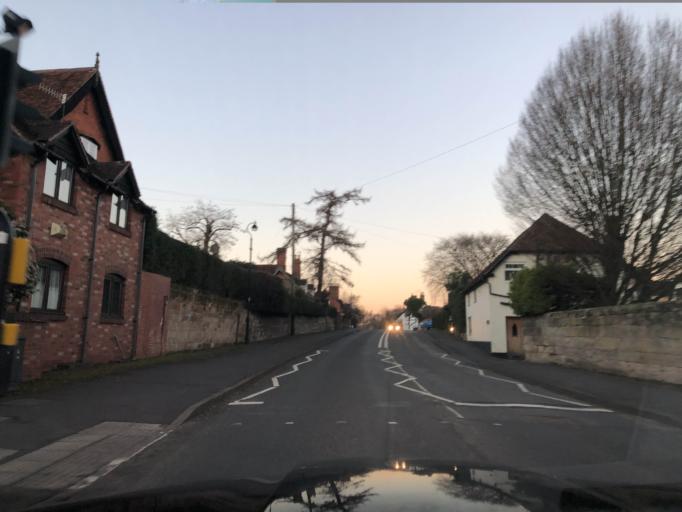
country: GB
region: England
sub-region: Warwickshire
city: Kenilworth
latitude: 52.3168
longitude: -1.5768
